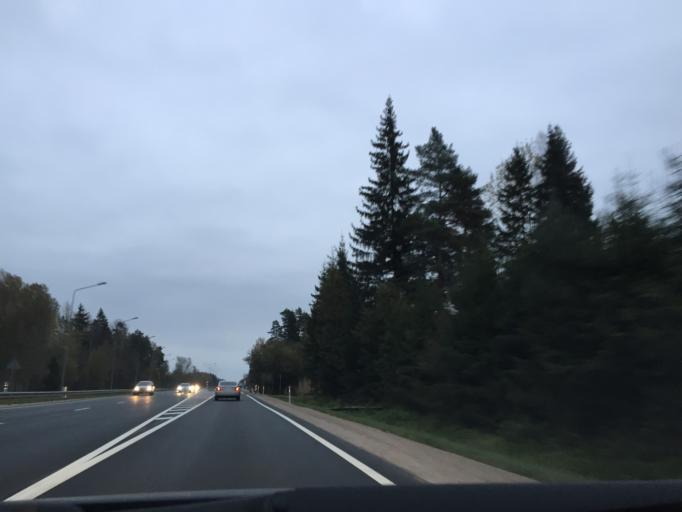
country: LV
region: Olaine
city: Olaine
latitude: 56.7344
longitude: 23.8666
